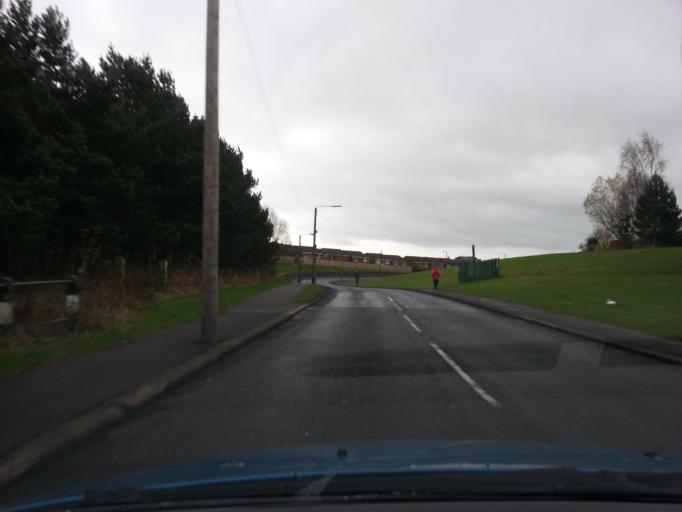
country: GB
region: England
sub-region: County Durham
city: Crook
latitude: 54.7202
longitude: -1.7488
